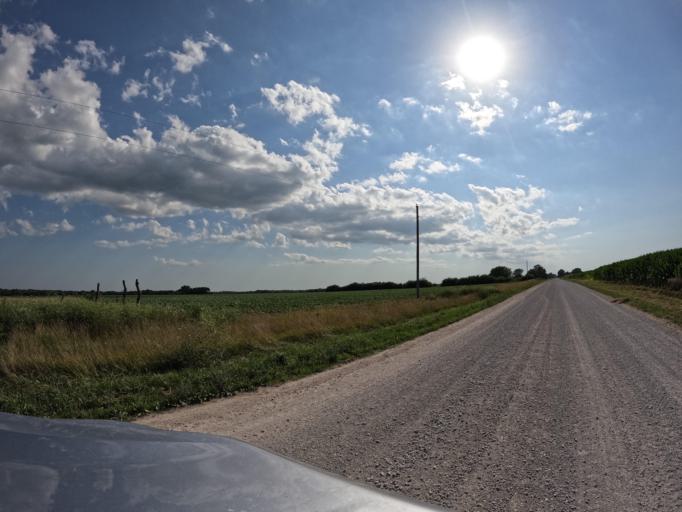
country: US
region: Iowa
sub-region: Appanoose County
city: Centerville
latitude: 40.7179
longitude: -93.0088
